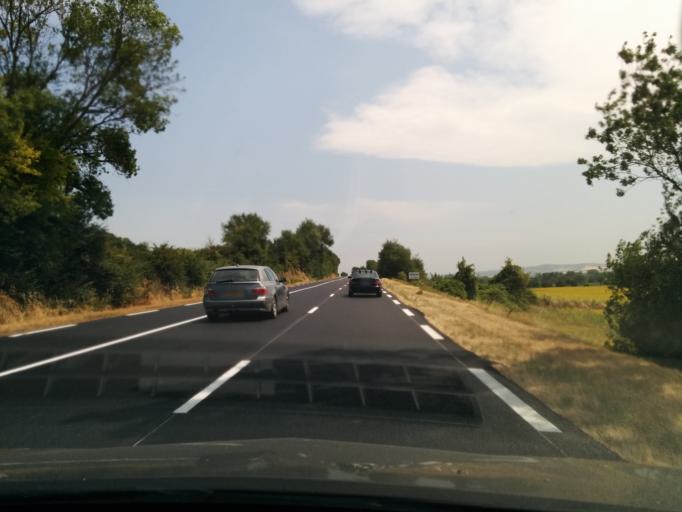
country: FR
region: Languedoc-Roussillon
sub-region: Departement de l'Aude
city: Bram
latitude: 43.2705
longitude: 2.1127
